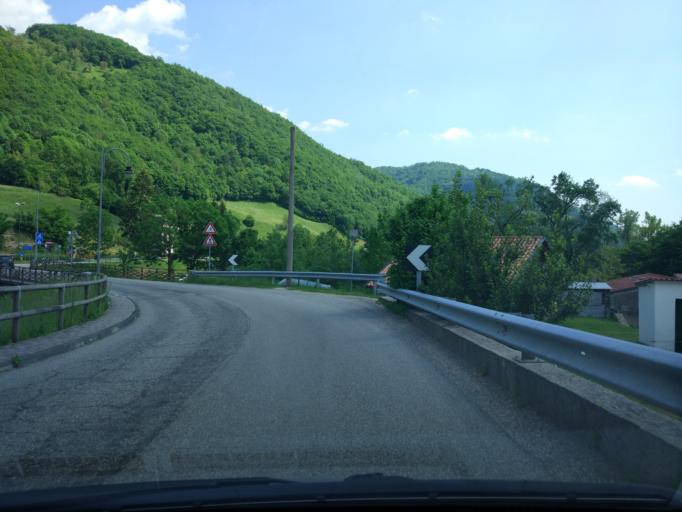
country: IT
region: Veneto
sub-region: Provincia di Verona
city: Selva di Progno
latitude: 45.5940
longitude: 11.1510
